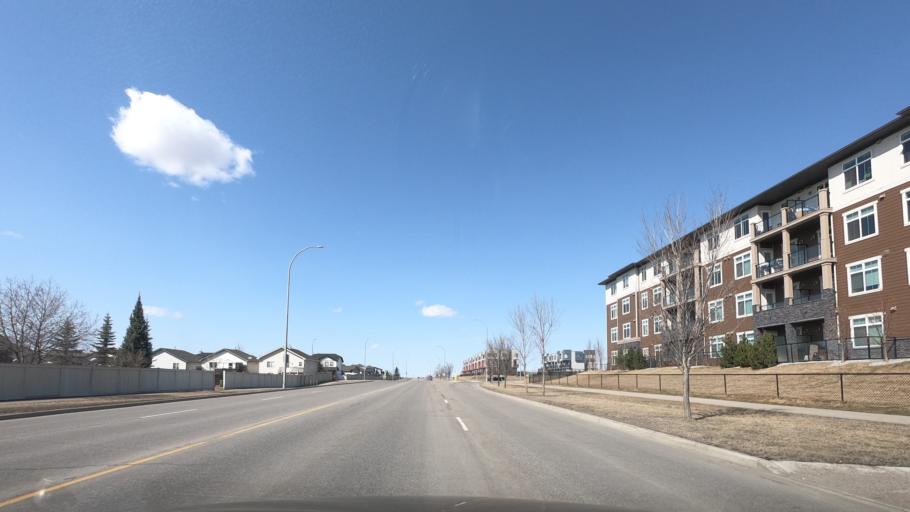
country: CA
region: Alberta
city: Airdrie
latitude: 51.3042
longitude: -114.0133
